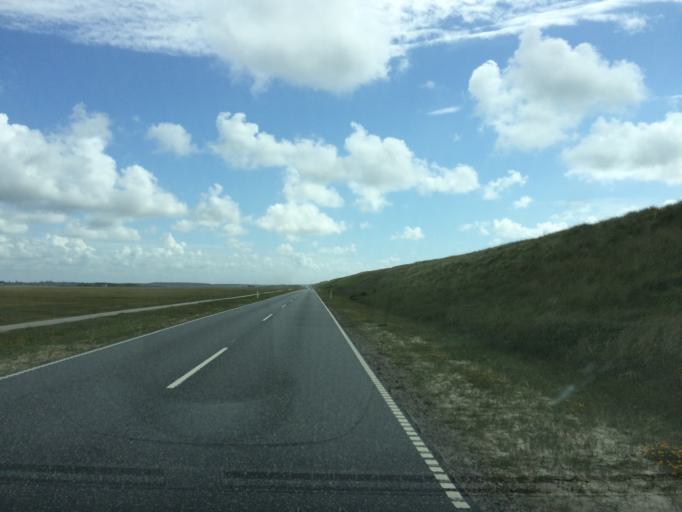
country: DK
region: Central Jutland
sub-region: Holstebro Kommune
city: Ulfborg
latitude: 56.3493
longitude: 8.1224
